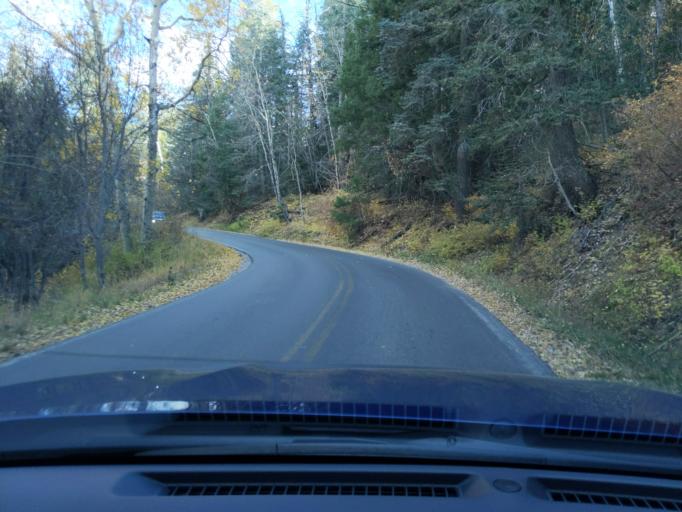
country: US
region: Arizona
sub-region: Pima County
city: Catalina
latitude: 32.4415
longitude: -110.7860
